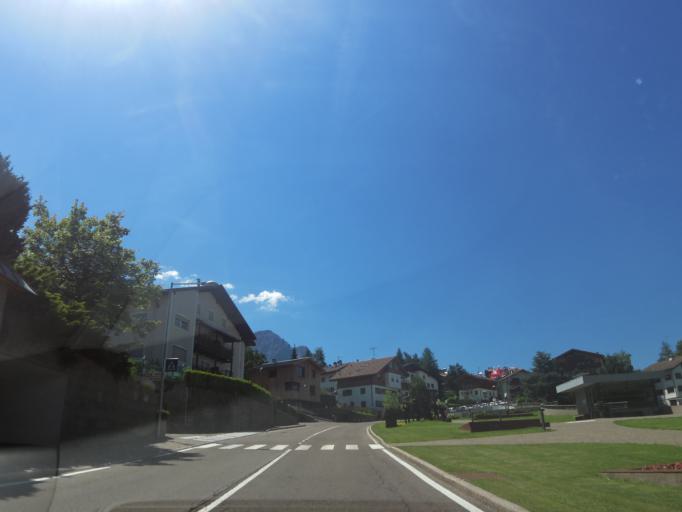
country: IT
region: Trentino-Alto Adige
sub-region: Bolzano
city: Castelrotto
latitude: 46.5658
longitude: 11.5590
